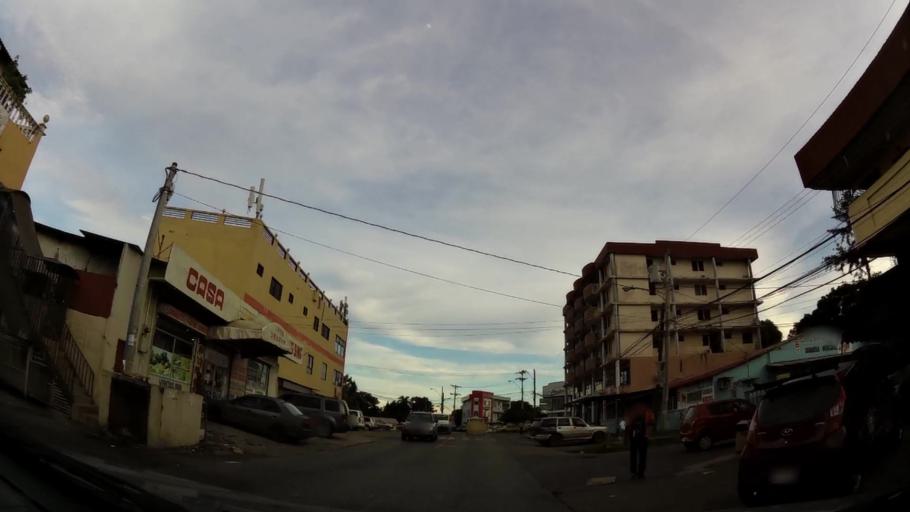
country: PA
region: Panama
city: La Chorrera
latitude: 8.8780
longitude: -79.7807
